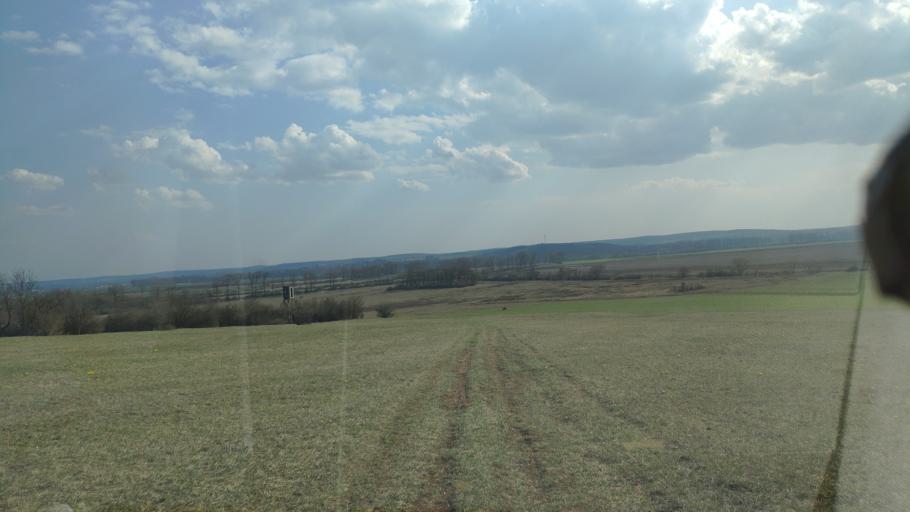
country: SK
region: Kosicky
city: Medzev
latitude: 48.6189
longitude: 20.9079
